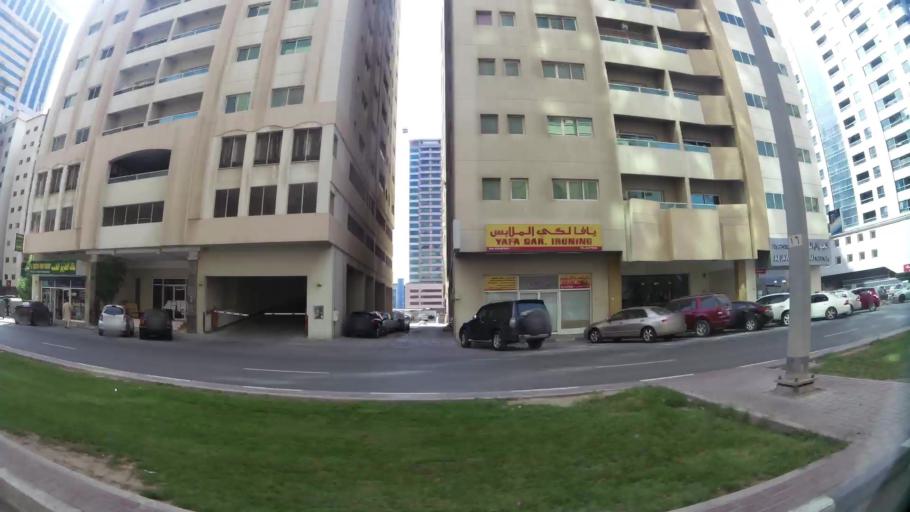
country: AE
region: Ash Shariqah
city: Sharjah
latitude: 25.3117
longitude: 55.3756
